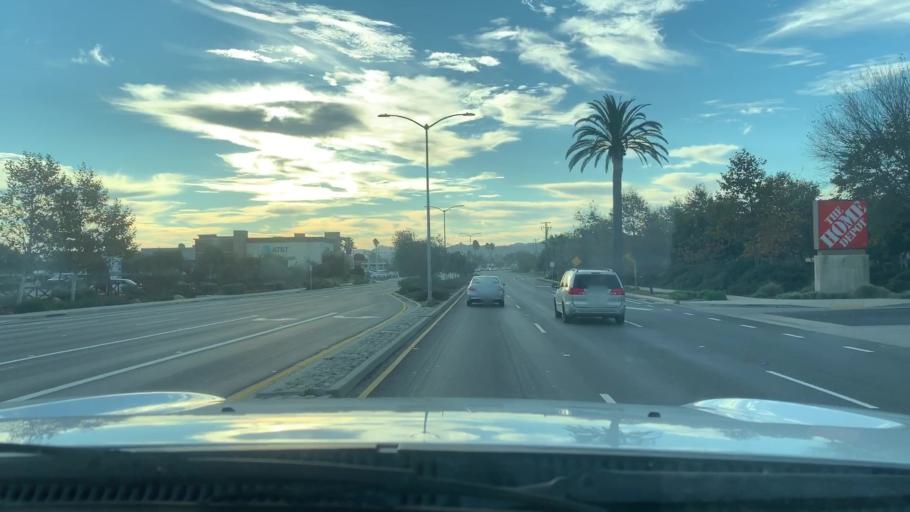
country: US
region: California
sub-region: San Luis Obispo County
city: San Luis Obispo
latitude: 35.2520
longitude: -120.6871
